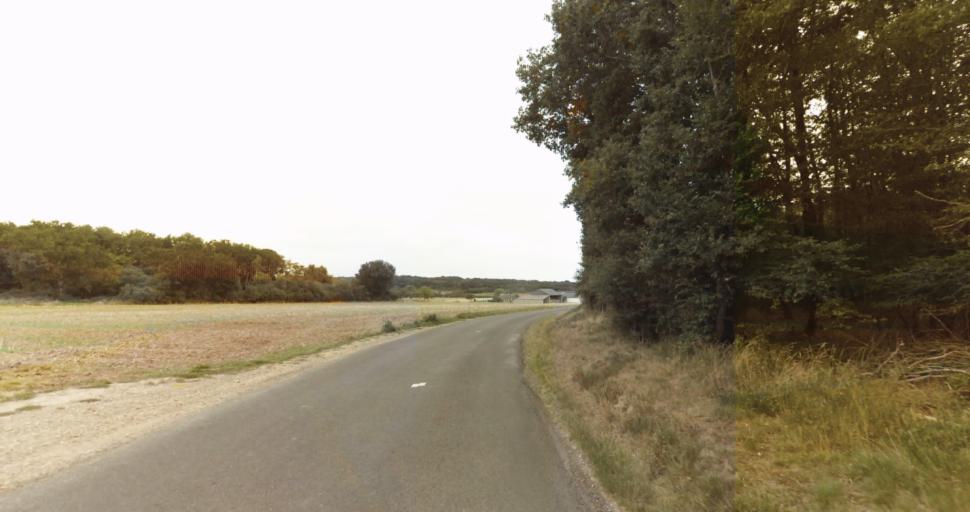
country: FR
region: Haute-Normandie
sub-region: Departement de l'Eure
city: Evreux
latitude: 48.9843
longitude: 1.2336
